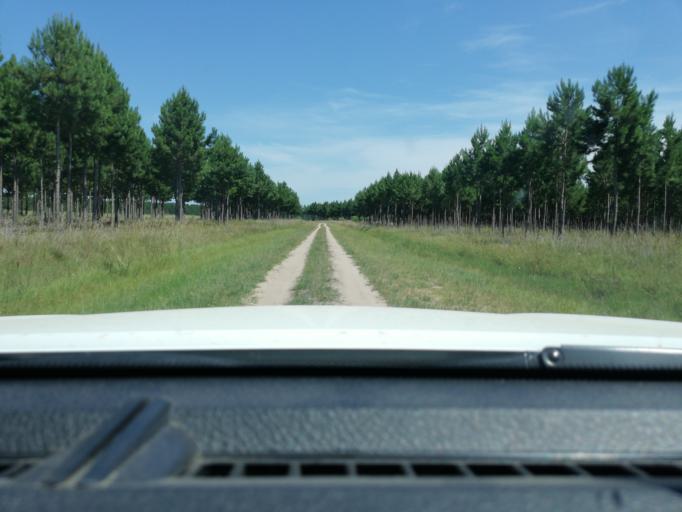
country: AR
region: Corrientes
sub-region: Departamento de San Miguel
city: San Miguel
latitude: -28.0325
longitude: -57.4683
